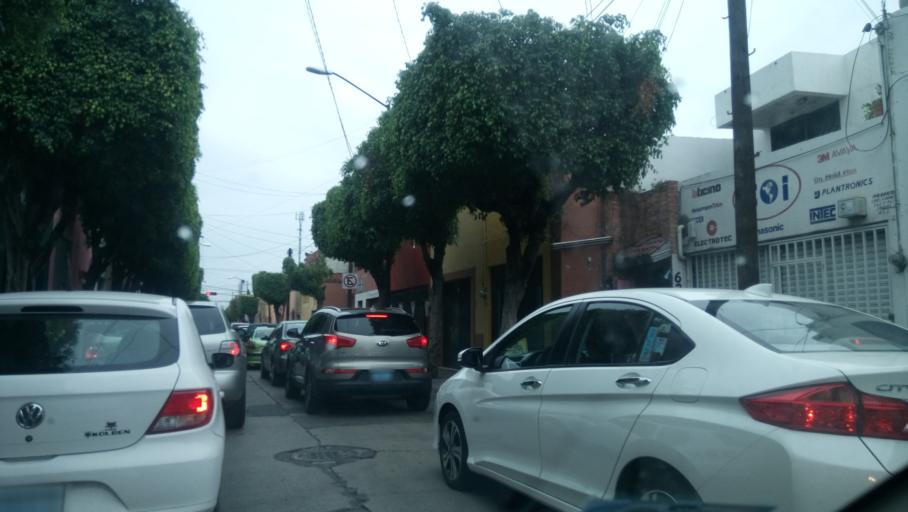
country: MX
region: Guanajuato
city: Leon
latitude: 21.1195
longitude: -101.6772
